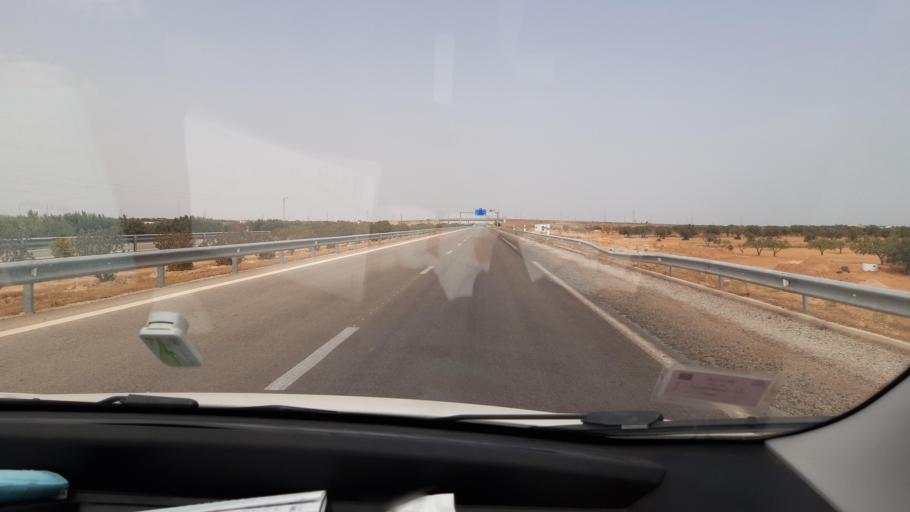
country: TN
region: Safaqis
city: Sfax
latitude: 34.8871
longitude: 10.7114
